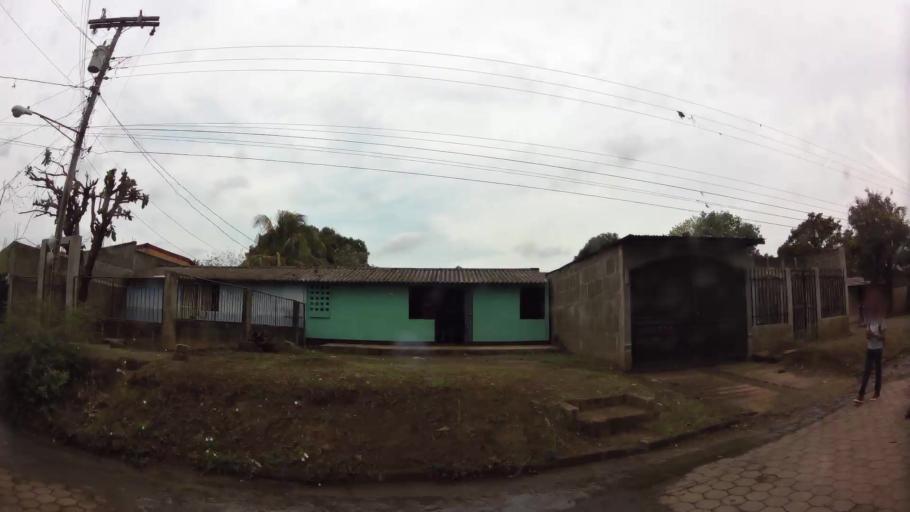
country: NI
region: Granada
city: Nandaime
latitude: 11.7574
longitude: -86.0579
